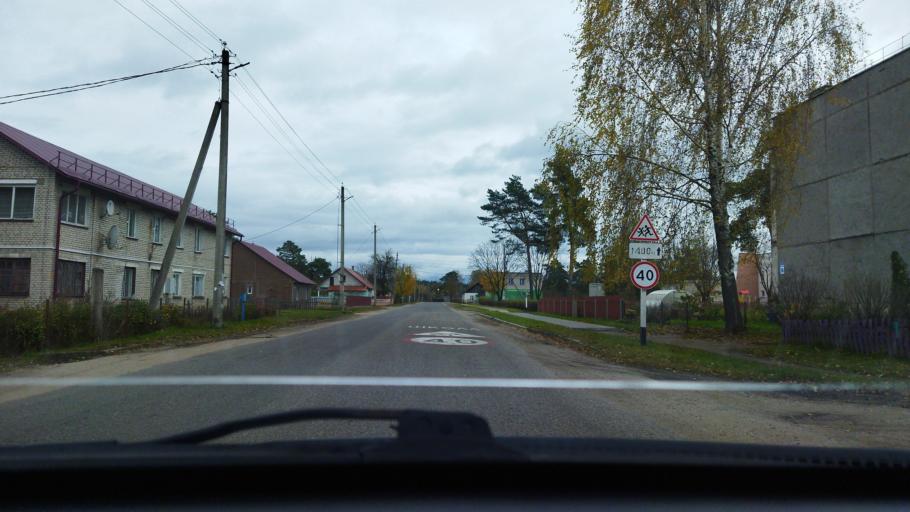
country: BY
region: Minsk
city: Svir
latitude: 54.8084
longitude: 26.2281
